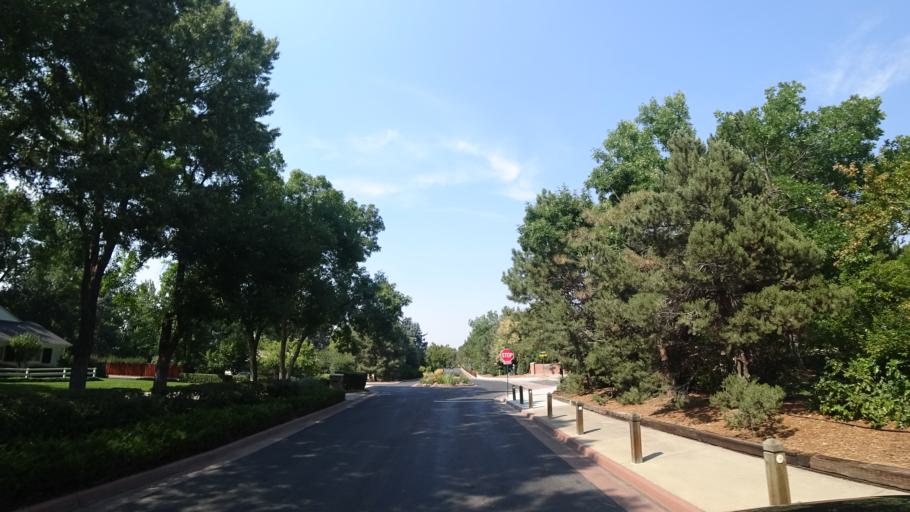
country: US
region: Colorado
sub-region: Arapahoe County
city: Greenwood Village
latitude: 39.6206
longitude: -104.9786
